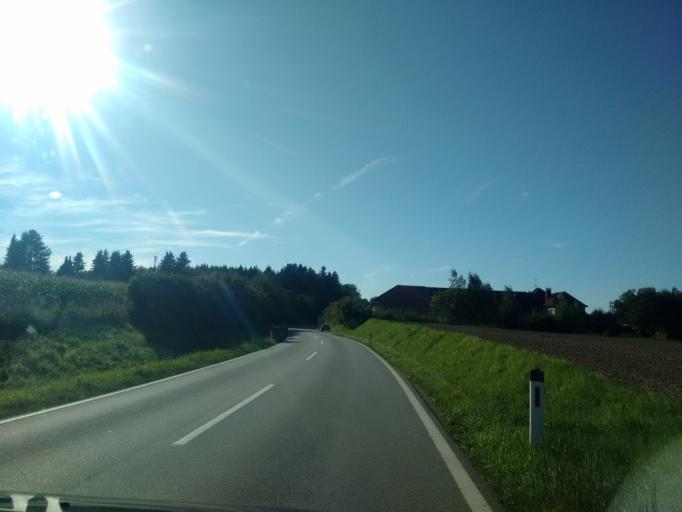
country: AT
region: Upper Austria
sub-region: Politischer Bezirk Kirchdorf an der Krems
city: Kremsmunster
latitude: 48.1094
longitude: 14.1041
